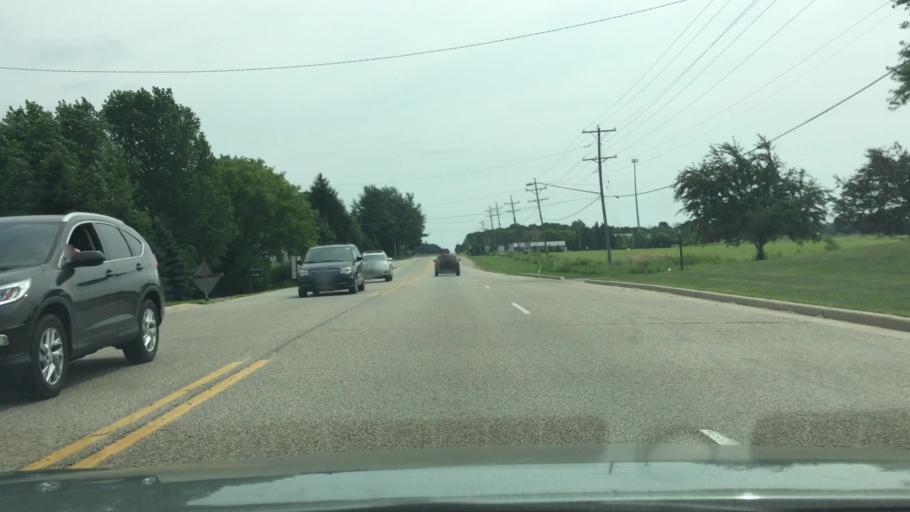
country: US
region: Wisconsin
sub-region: Waukesha County
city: Merton
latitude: 43.1413
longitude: -88.3033
